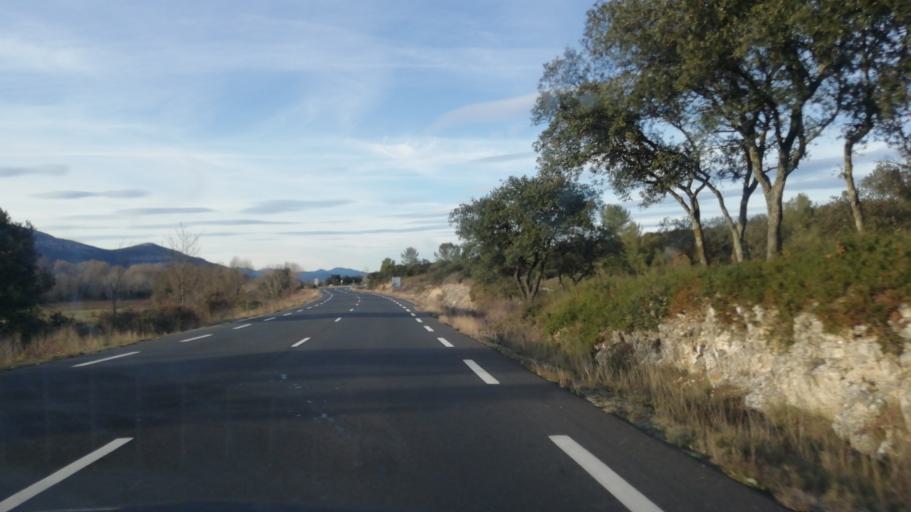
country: FR
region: Languedoc-Roussillon
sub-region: Departement du Gard
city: Quissac
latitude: 43.8892
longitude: 4.0141
